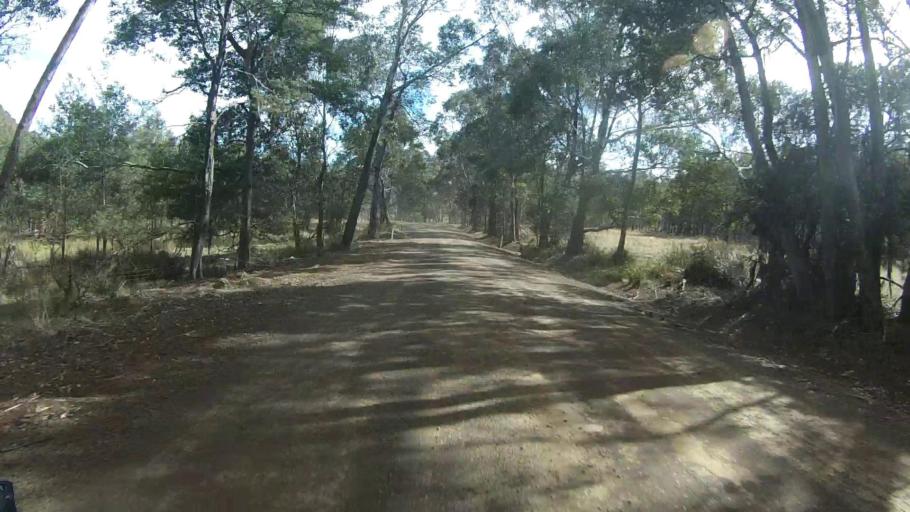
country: AU
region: Tasmania
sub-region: Sorell
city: Sorell
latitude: -42.6579
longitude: 147.8977
